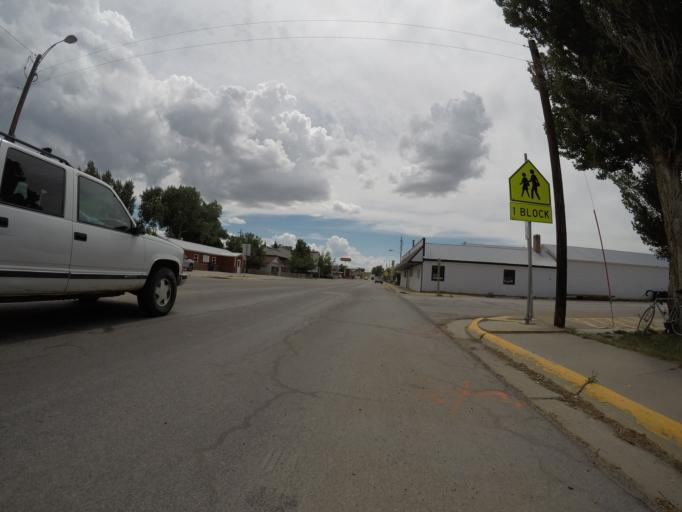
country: US
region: Wyoming
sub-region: Carbon County
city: Saratoga
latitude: 41.4541
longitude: -106.8077
